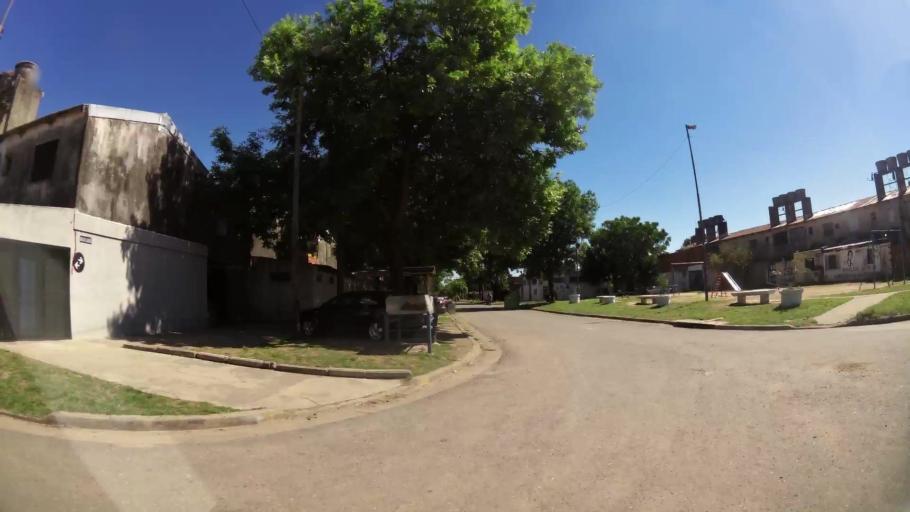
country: AR
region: Santa Fe
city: Perez
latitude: -32.9748
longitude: -60.7033
